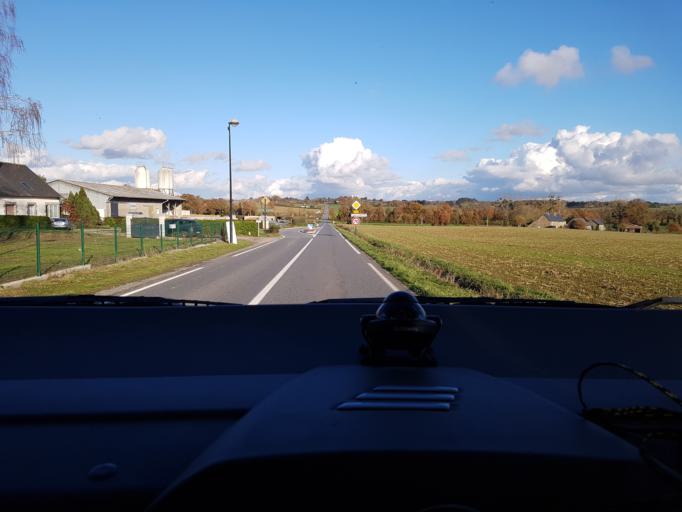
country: FR
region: Brittany
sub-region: Departement d'Ille-et-Vilaine
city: Pire-sur-Seiche
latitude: 48.0115
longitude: -1.4244
